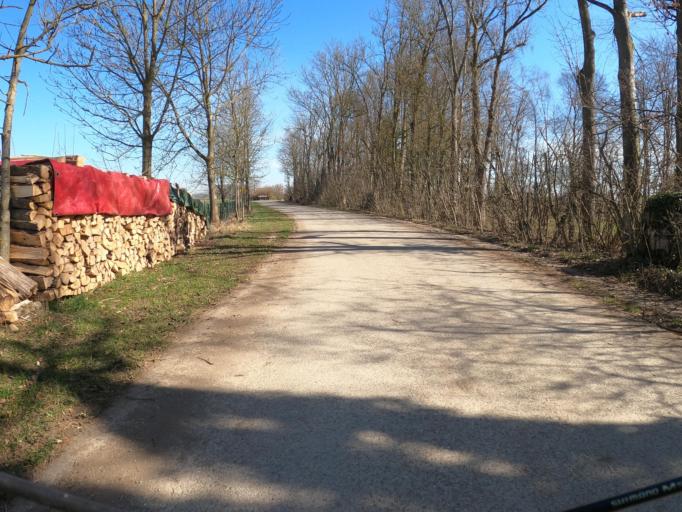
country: DE
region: Bavaria
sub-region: Swabia
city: Nersingen
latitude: 48.4520
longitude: 10.1519
